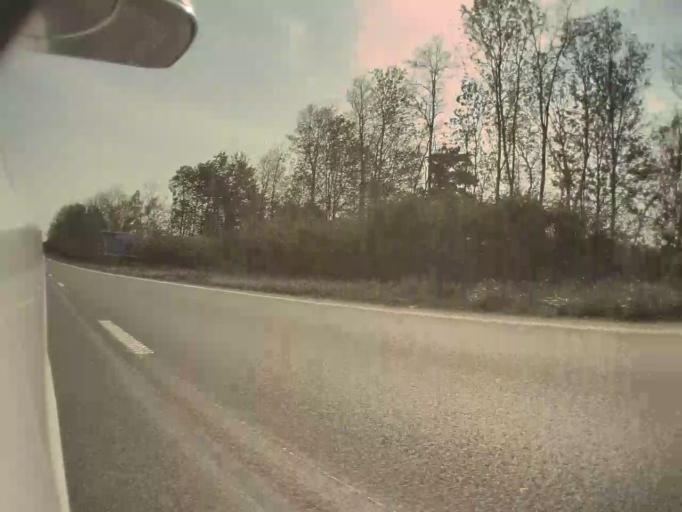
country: BE
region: Wallonia
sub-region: Province de Namur
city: Ciney
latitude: 50.3062
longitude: 5.1220
